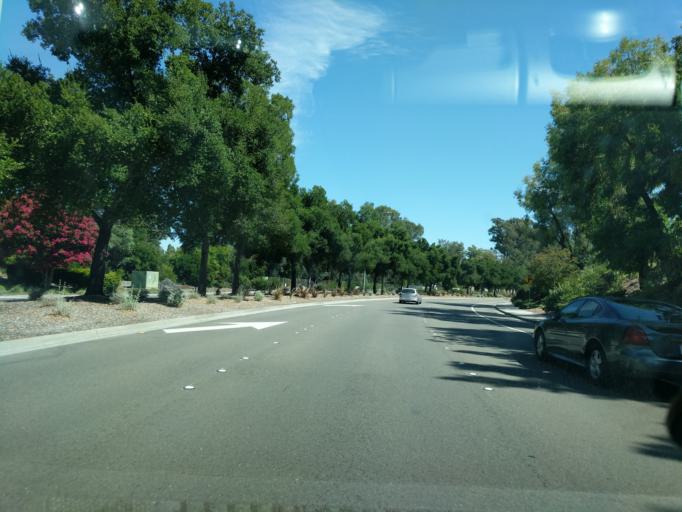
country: US
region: California
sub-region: Contra Costa County
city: San Ramon
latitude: 37.7569
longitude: -121.9646
